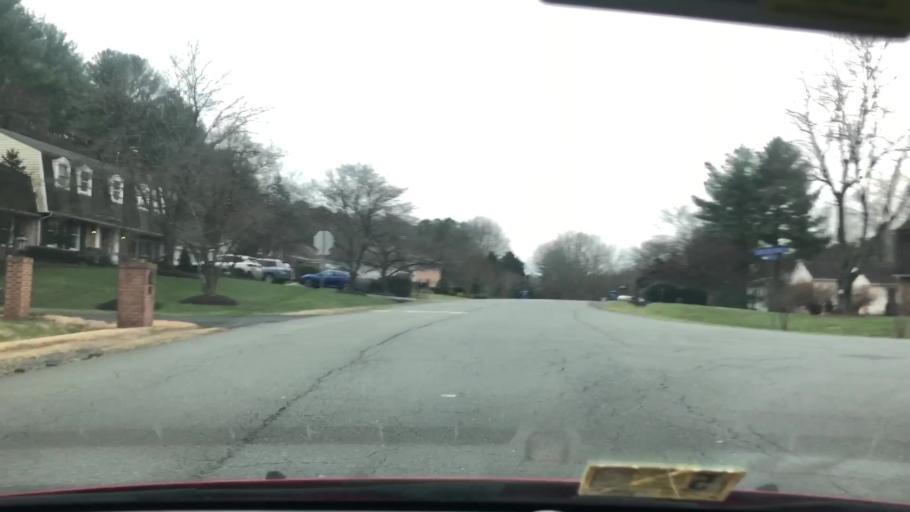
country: US
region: Virginia
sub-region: Fairfax County
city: Wolf Trap
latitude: 38.9615
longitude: -77.2738
